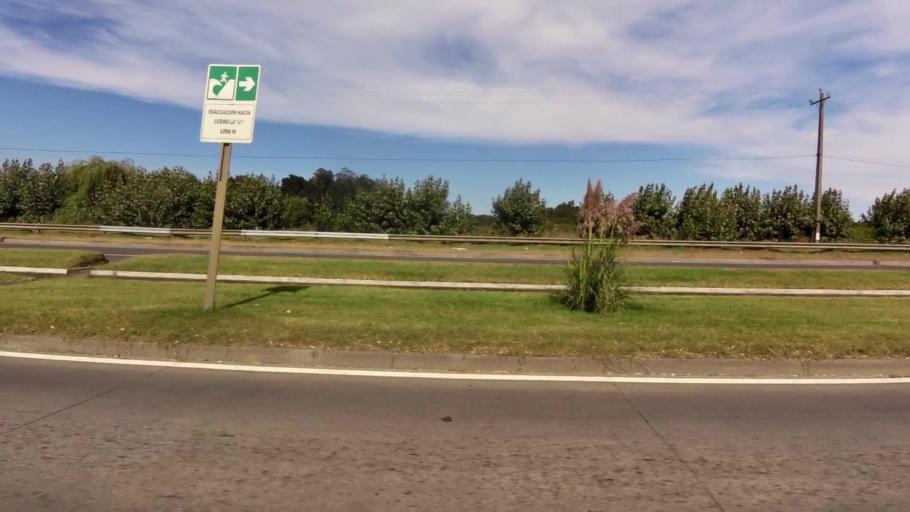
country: CL
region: Biobio
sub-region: Provincia de Concepcion
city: Talcahuano
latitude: -36.7652
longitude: -73.1168
